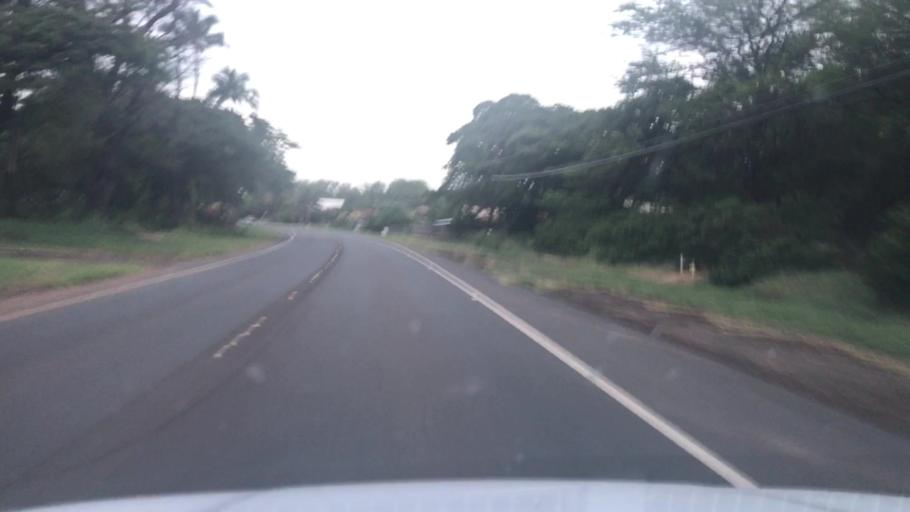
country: US
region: Hawaii
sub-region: Maui County
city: Kaunakakai
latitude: 21.0663
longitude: -156.9511
